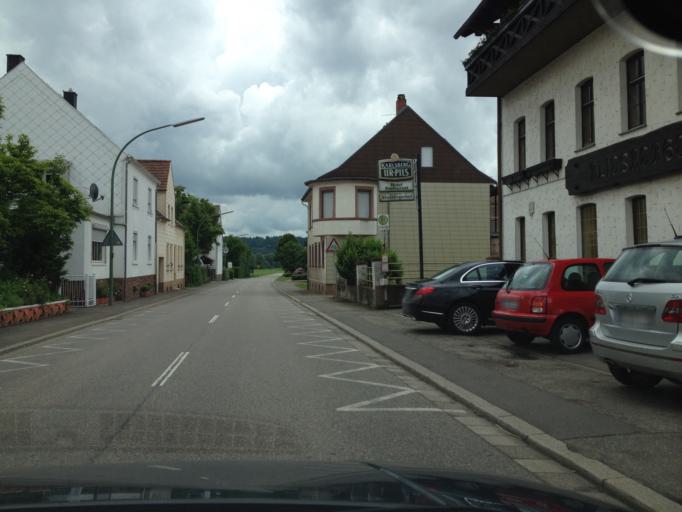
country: DE
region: Saarland
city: Homburg
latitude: 49.3083
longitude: 7.2940
